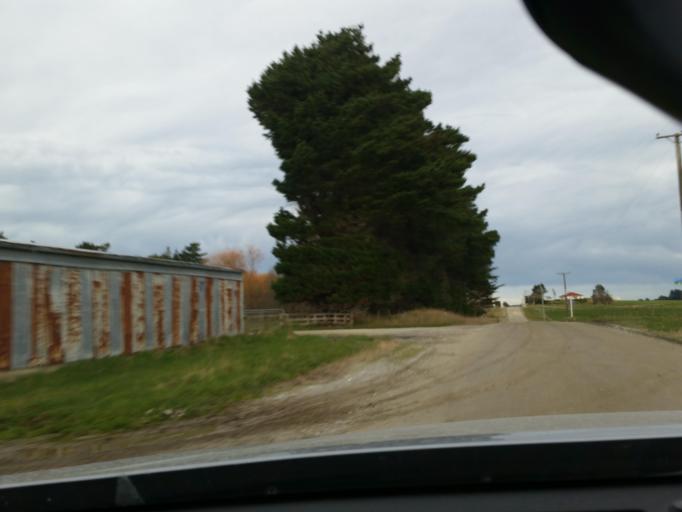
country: NZ
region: Southland
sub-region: Invercargill City
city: Invercargill
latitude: -46.4173
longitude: 168.5061
